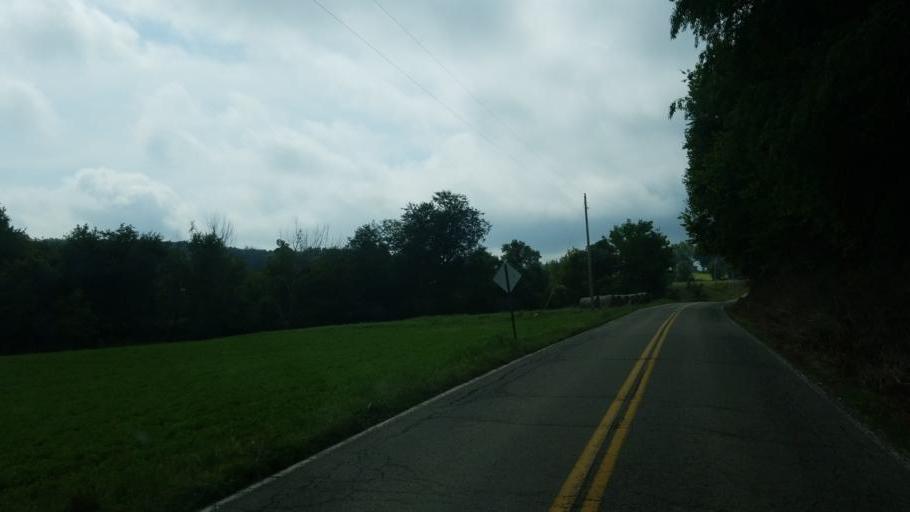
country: US
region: Ohio
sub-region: Licking County
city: Utica
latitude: 40.2231
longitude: -82.4571
